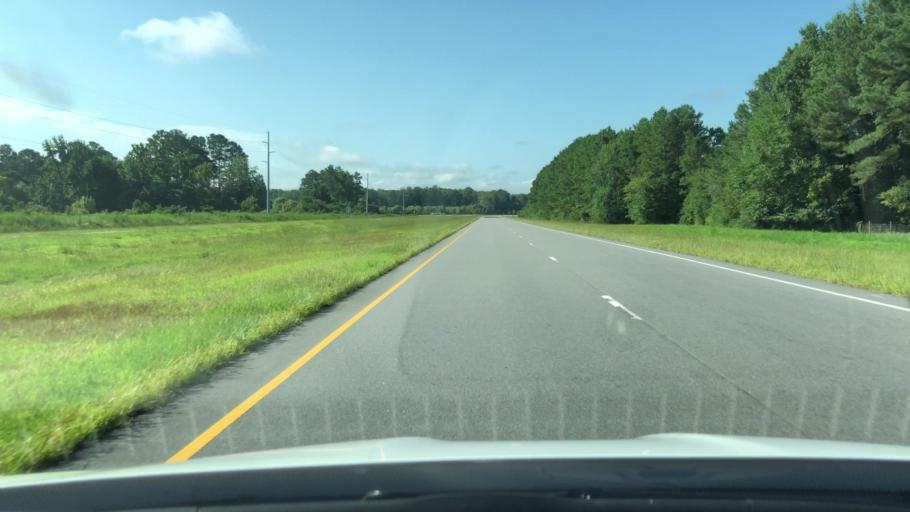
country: US
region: North Carolina
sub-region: Pasquotank County
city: Elizabeth City
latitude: 36.4414
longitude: -76.3391
